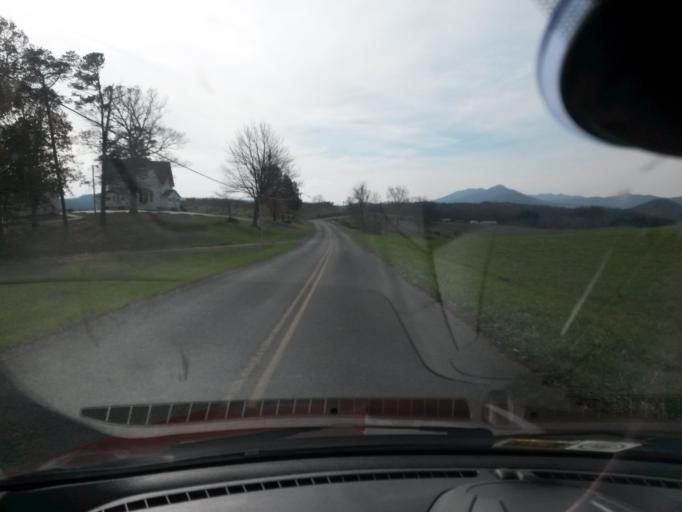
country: US
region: Virginia
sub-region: Botetourt County
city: Fincastle
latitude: 37.6185
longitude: -79.8358
